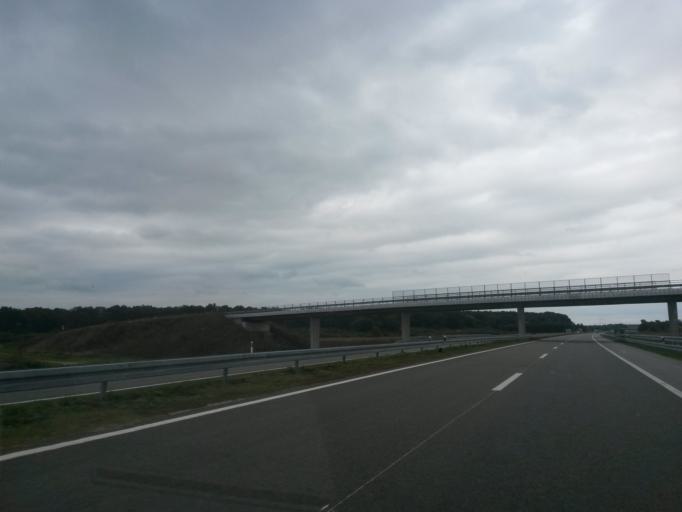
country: HR
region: Osjecko-Baranjska
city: Vuka
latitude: 45.4604
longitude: 18.4713
